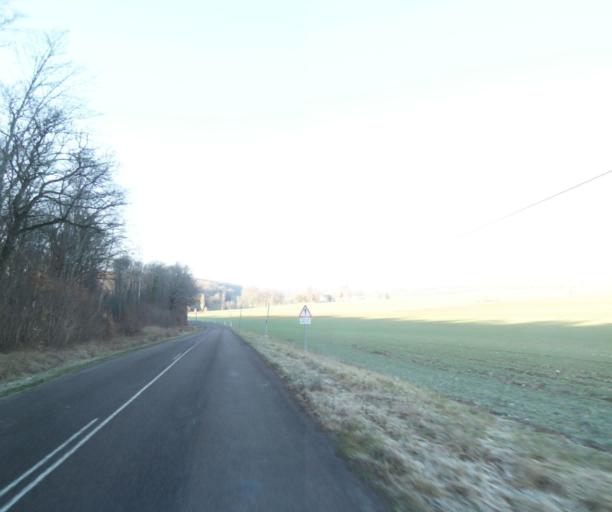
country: FR
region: Champagne-Ardenne
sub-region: Departement de la Haute-Marne
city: Chevillon
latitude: 48.5532
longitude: 5.0911
